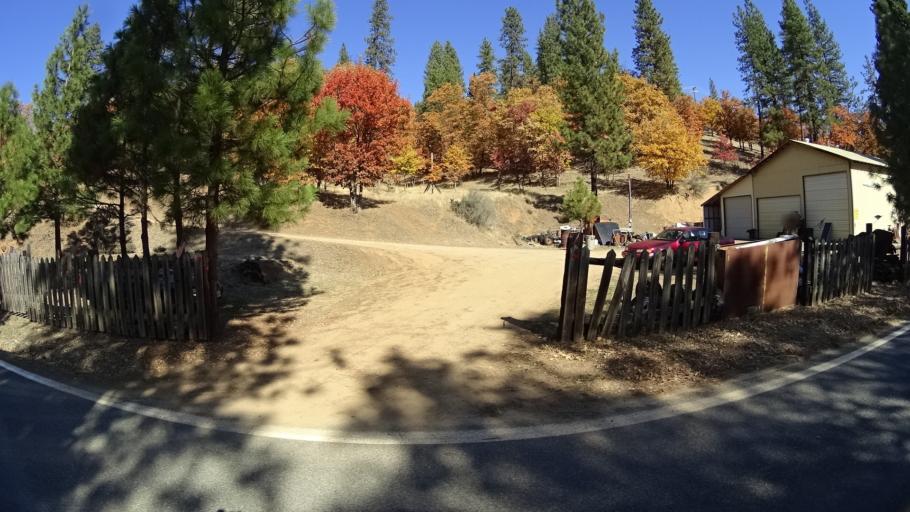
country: US
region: California
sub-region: Siskiyou County
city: Yreka
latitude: 41.6322
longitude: -122.9558
